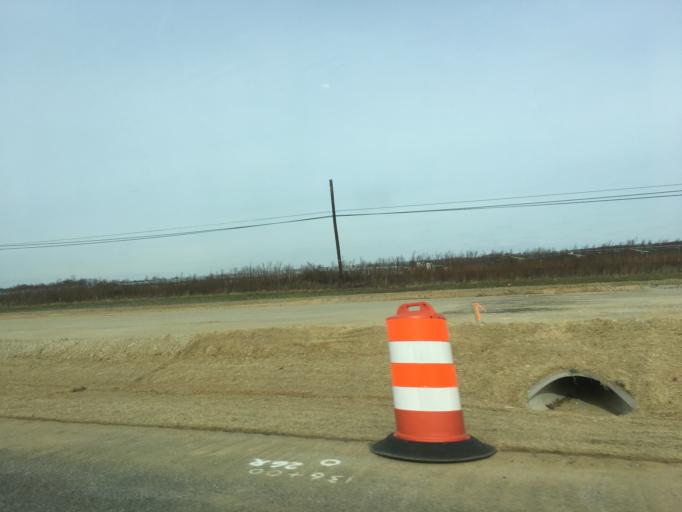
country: US
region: Maryland
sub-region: Queen Anne's County
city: Centreville
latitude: 38.9355
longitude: -76.0416
